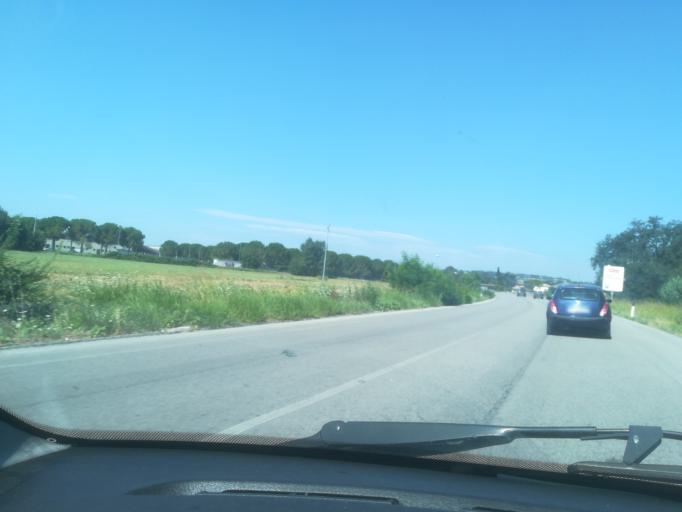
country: IT
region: The Marches
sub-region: Provincia di Macerata
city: Villa Potenza
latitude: 43.3342
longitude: 13.4360
